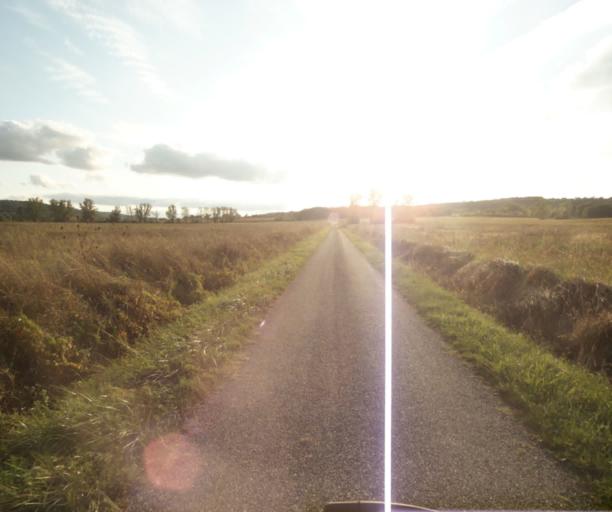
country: FR
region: Midi-Pyrenees
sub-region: Departement de la Haute-Garonne
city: Launac
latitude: 43.8280
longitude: 1.1334
